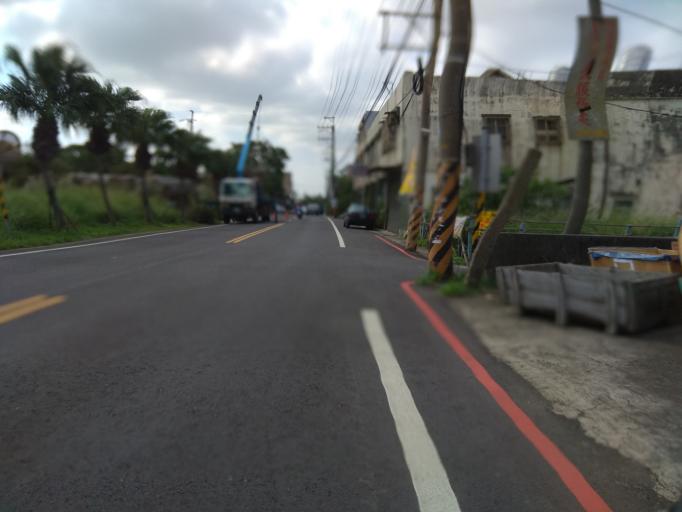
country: TW
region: Taiwan
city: Taoyuan City
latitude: 25.0619
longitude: 121.2358
